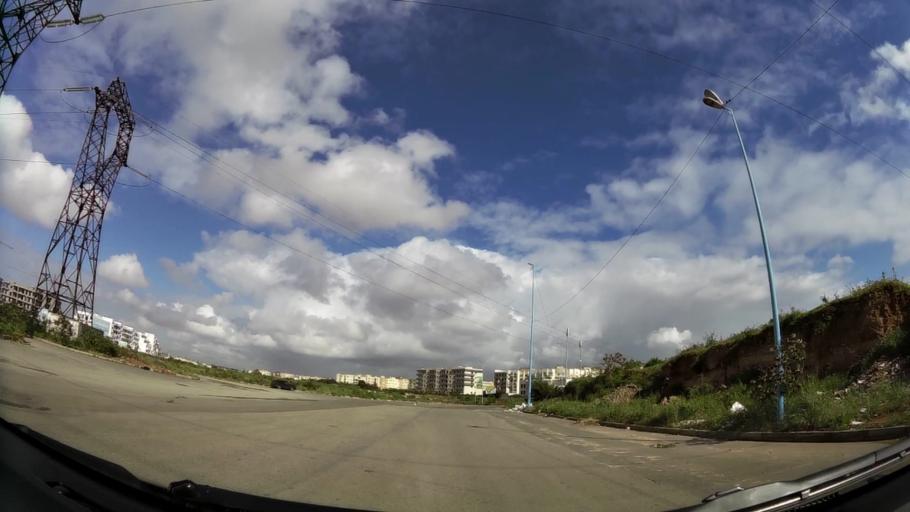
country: MA
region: Grand Casablanca
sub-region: Casablanca
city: Casablanca
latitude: 33.5399
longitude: -7.6168
